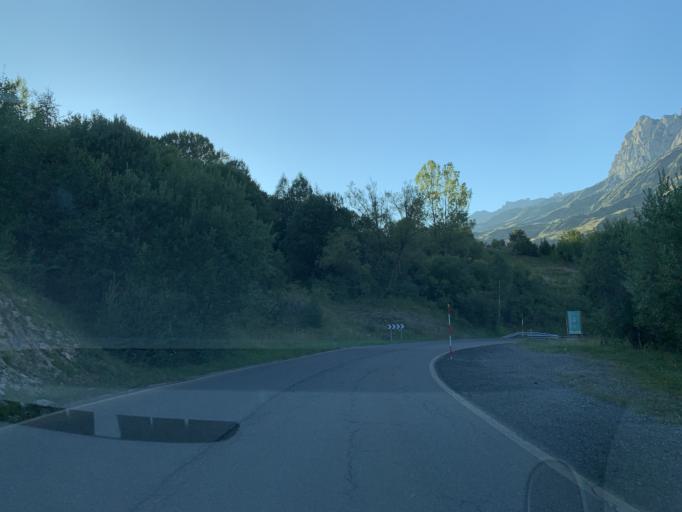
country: ES
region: Aragon
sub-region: Provincia de Huesca
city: Sallent de Gallego
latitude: 42.7624
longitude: -0.3355
